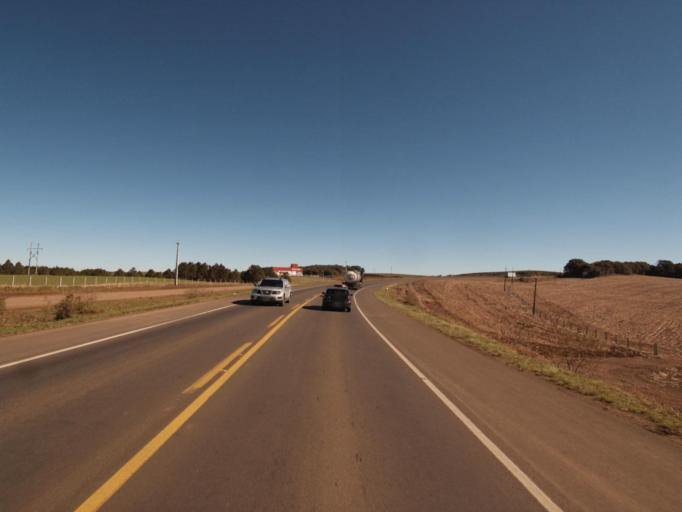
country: BR
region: Santa Catarina
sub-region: Xanxere
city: Xanxere
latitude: -26.8745
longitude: -52.2827
